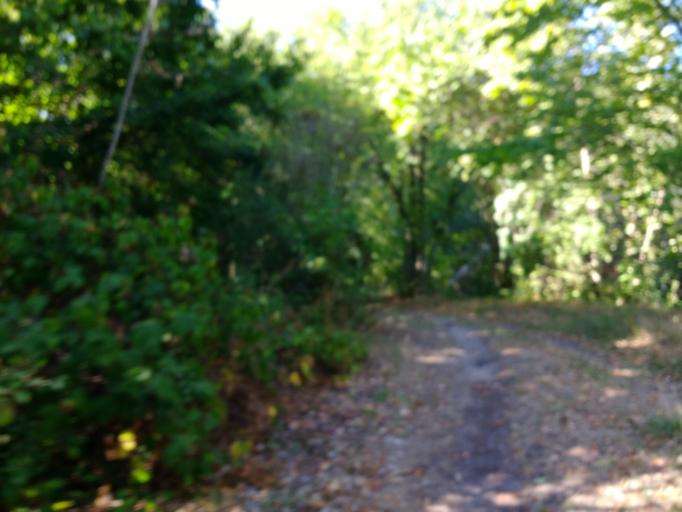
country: DE
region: Lower Saxony
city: Gifhorn
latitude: 52.4594
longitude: 10.5435
